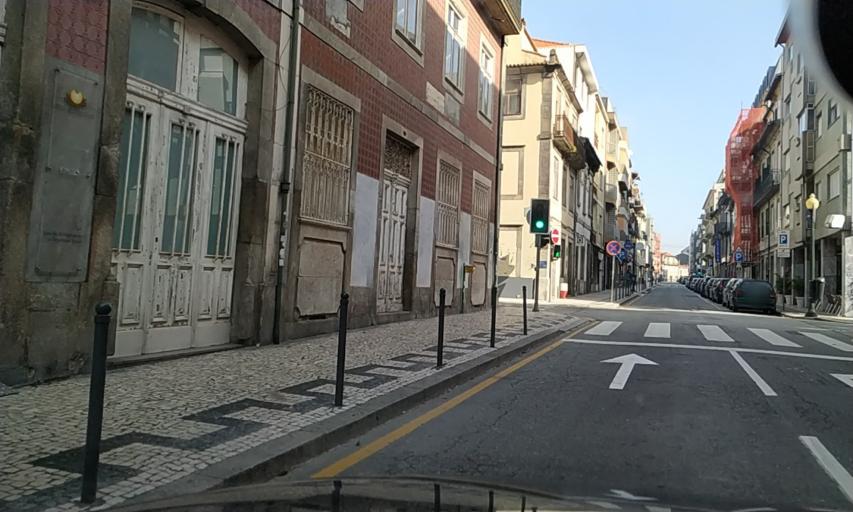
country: PT
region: Porto
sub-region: Porto
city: Porto
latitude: 41.1494
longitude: -8.6208
